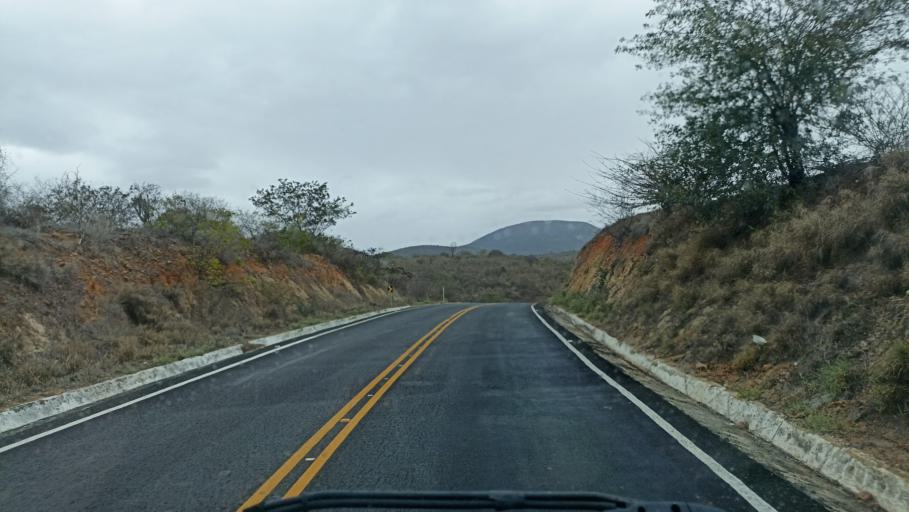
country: BR
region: Bahia
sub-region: Andarai
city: Vera Cruz
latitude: -13.0493
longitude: -40.7533
